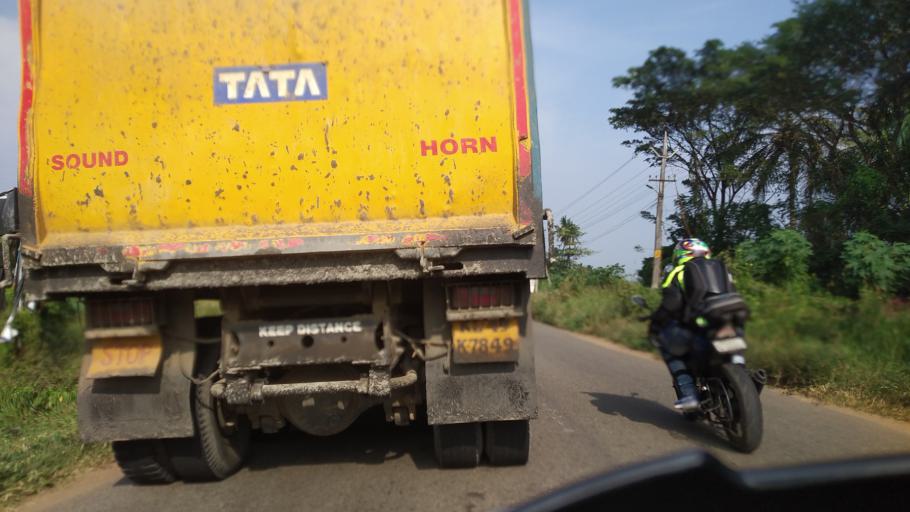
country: IN
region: Kerala
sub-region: Thrissur District
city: Chelakara
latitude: 10.5922
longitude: 76.5195
